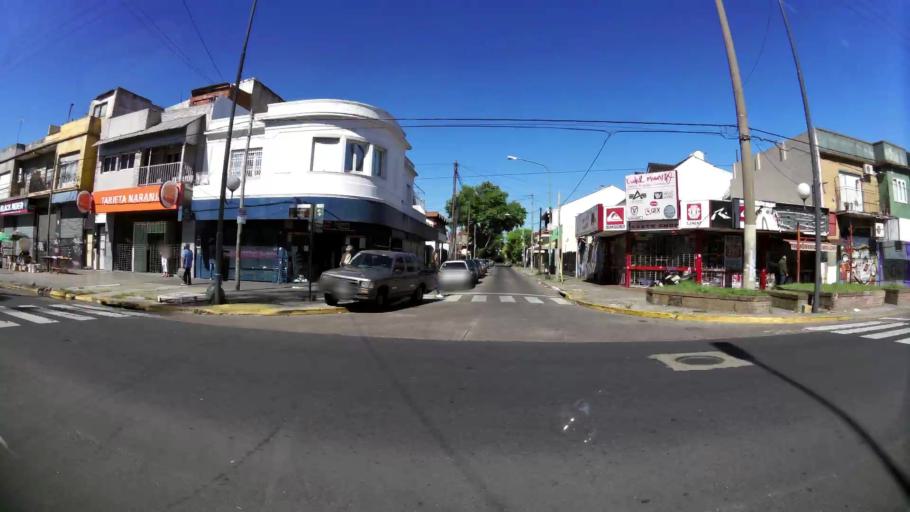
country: AR
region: Buenos Aires
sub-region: Partido de Vicente Lopez
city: Olivos
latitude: -34.5289
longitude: -58.5167
